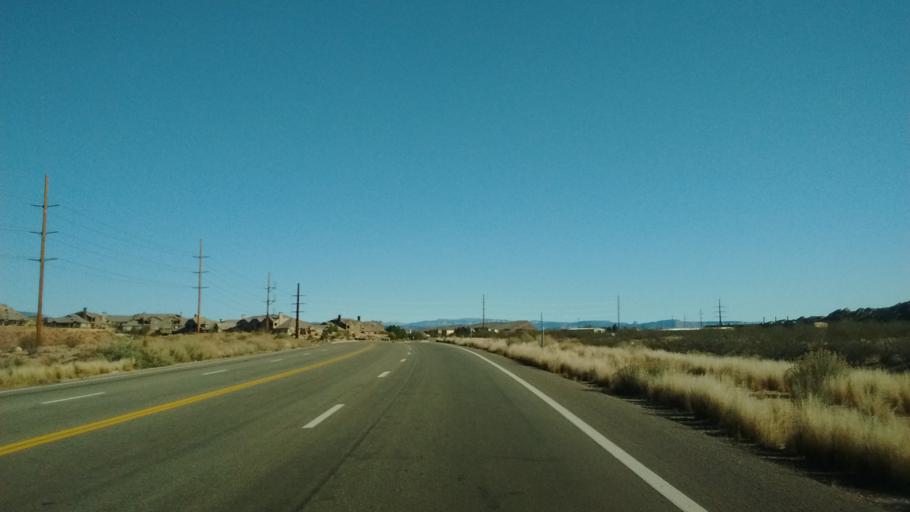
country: US
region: Utah
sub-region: Washington County
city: Washington
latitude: 37.1535
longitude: -113.4441
